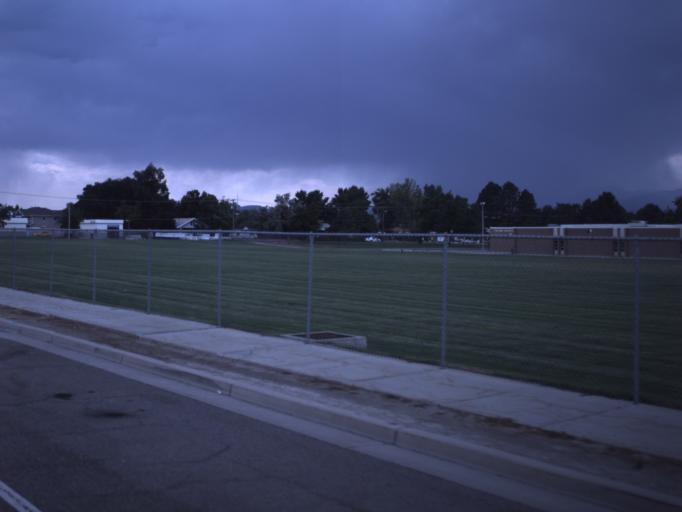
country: US
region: Utah
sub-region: Salt Lake County
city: Sandy City
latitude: 40.6076
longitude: -111.8723
